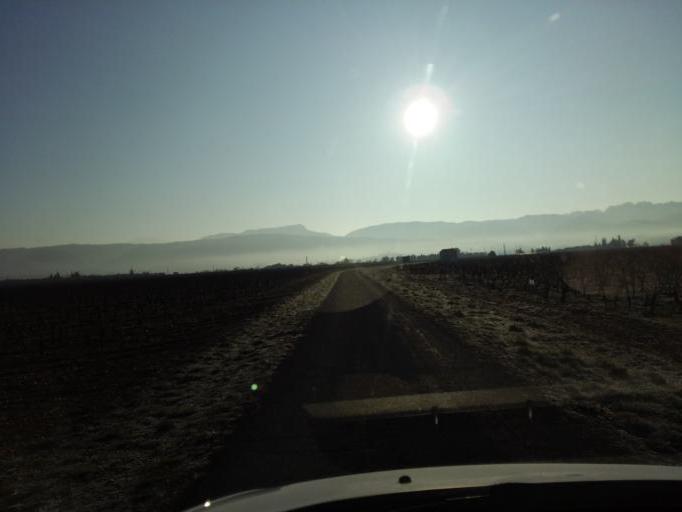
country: FR
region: Provence-Alpes-Cote d'Azur
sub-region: Departement du Vaucluse
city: Sablet
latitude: 44.2064
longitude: 4.9767
